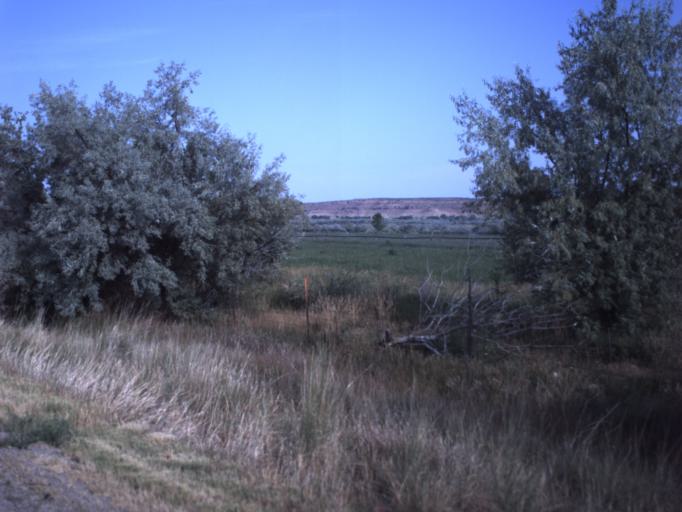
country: US
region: Utah
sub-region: Duchesne County
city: Roosevelt
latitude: 40.2583
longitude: -110.1170
